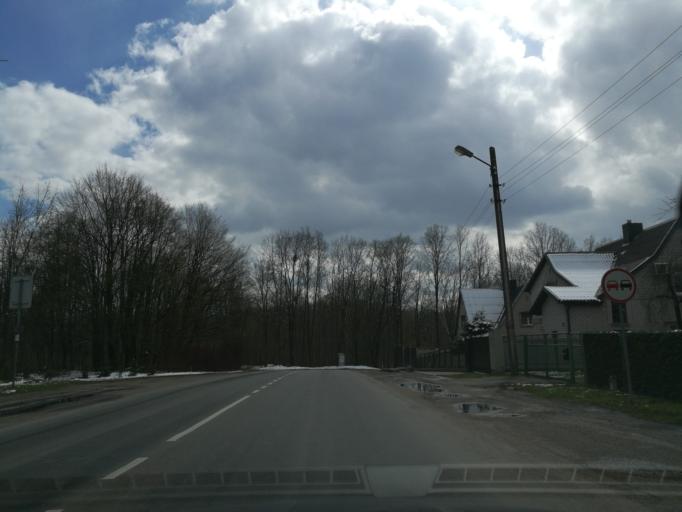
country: LT
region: Kauno apskritis
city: Dainava (Kaunas)
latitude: 54.8638
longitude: 24.0003
